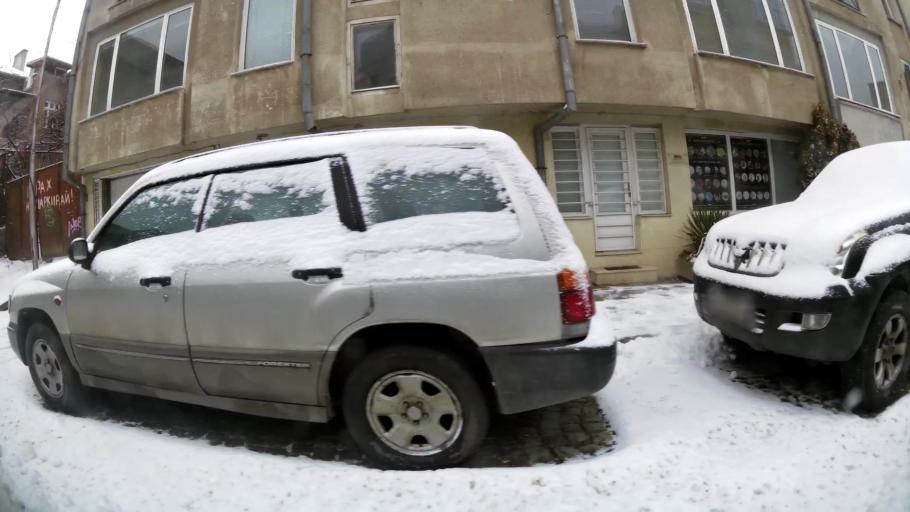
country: BG
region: Sofia-Capital
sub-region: Stolichna Obshtina
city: Sofia
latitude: 42.6965
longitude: 23.3131
